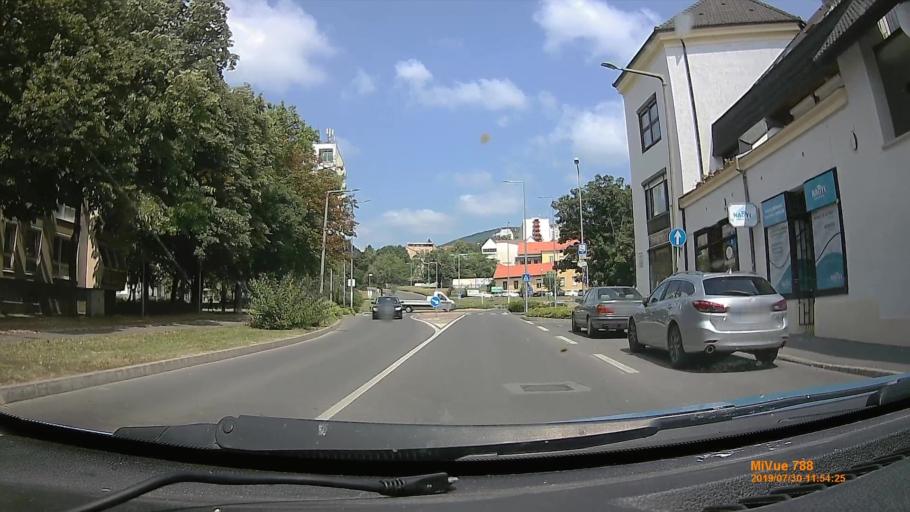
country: HU
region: Baranya
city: Pecs
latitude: 46.0764
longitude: 18.2147
